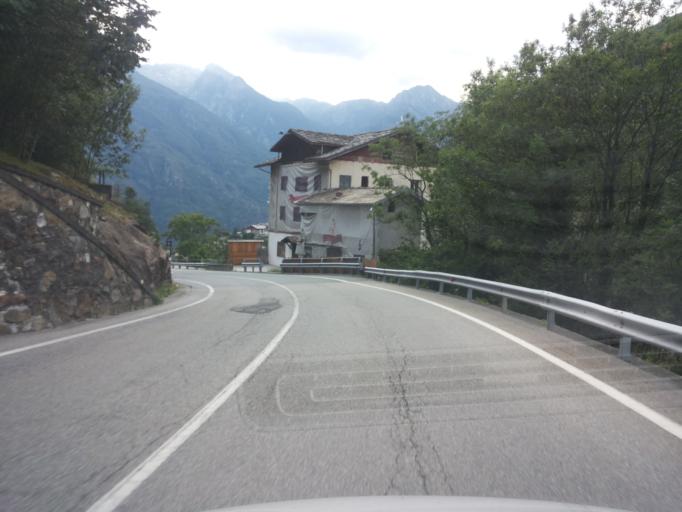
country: IT
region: Aosta Valley
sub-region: Valle d'Aosta
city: Perloz
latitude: 45.6076
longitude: 7.8111
